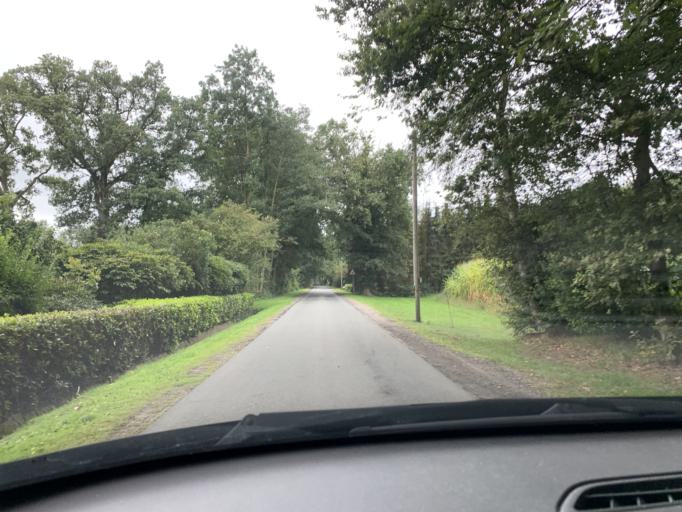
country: DE
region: Lower Saxony
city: Westerstede
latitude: 53.2797
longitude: 7.8889
